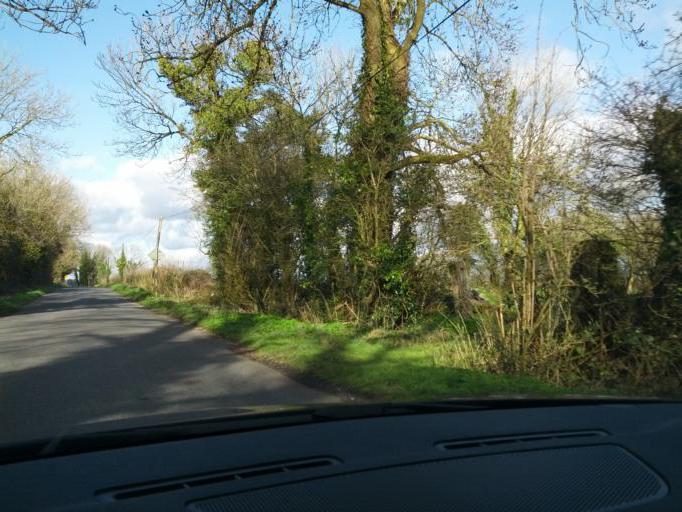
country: IE
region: Connaught
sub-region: County Galway
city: Athenry
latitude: 53.4681
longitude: -8.5708
